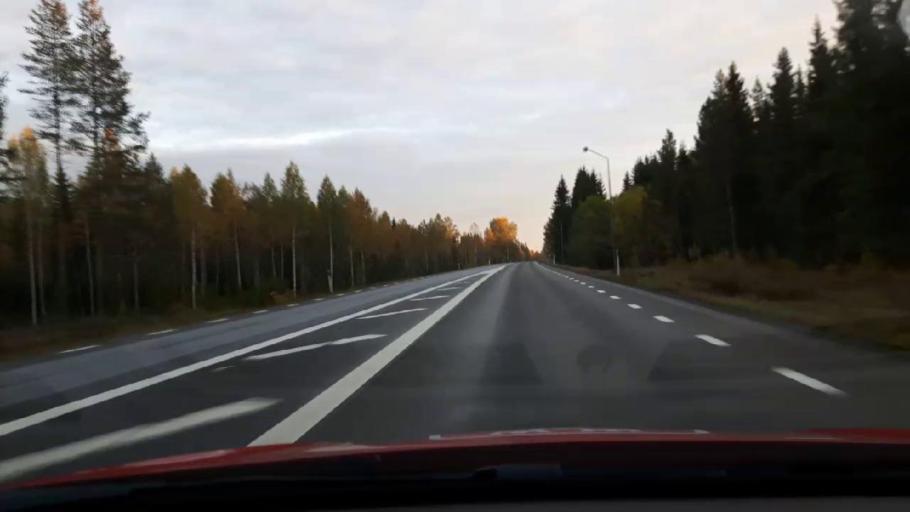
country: SE
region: Jaemtland
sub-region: OEstersunds Kommun
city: Lit
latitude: 63.2966
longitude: 14.8688
